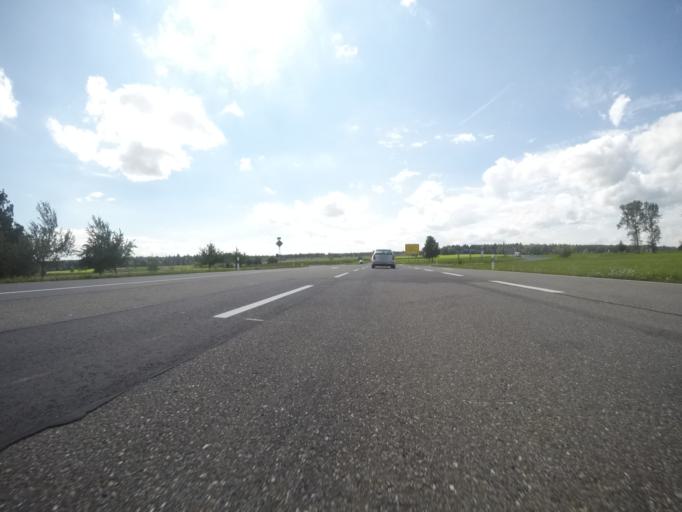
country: DE
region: Baden-Wuerttemberg
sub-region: Karlsruhe Region
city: Pfalzgrafenweiler
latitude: 48.5223
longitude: 8.5434
